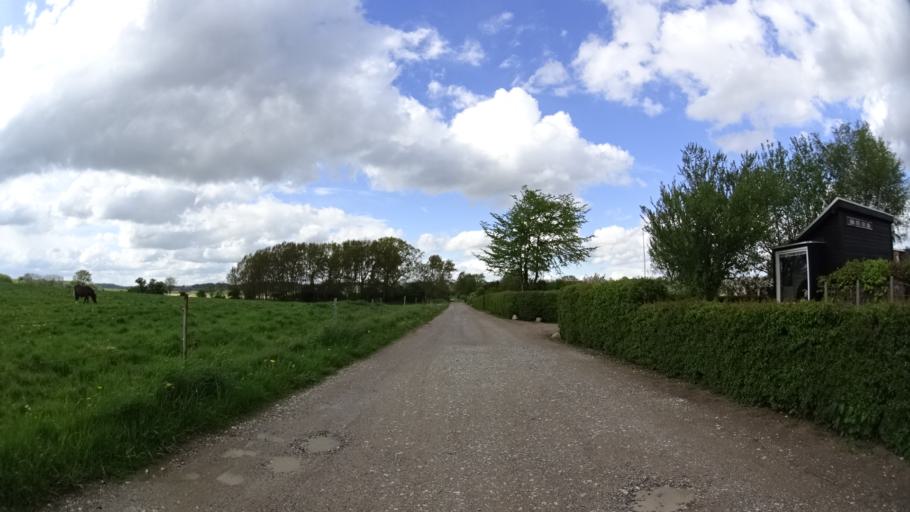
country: DK
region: Central Jutland
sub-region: Arhus Kommune
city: Stavtrup
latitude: 56.1344
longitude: 10.1414
